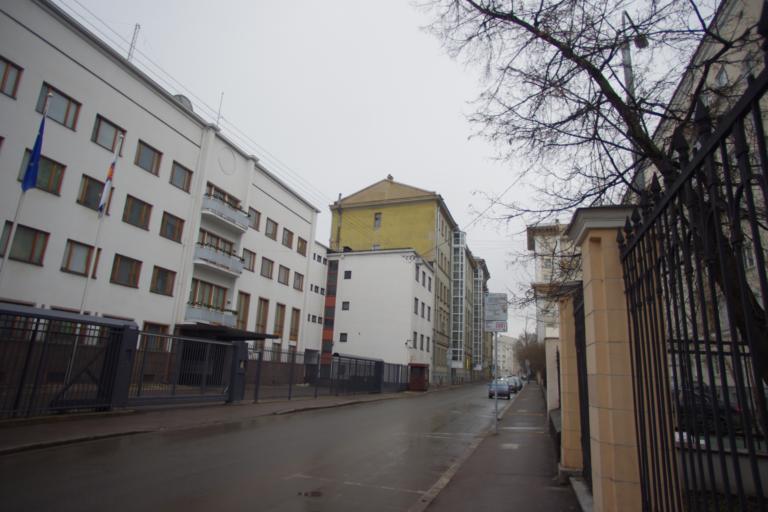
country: RU
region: Moskovskaya
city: Dorogomilovo
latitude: 55.7391
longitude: 37.5912
